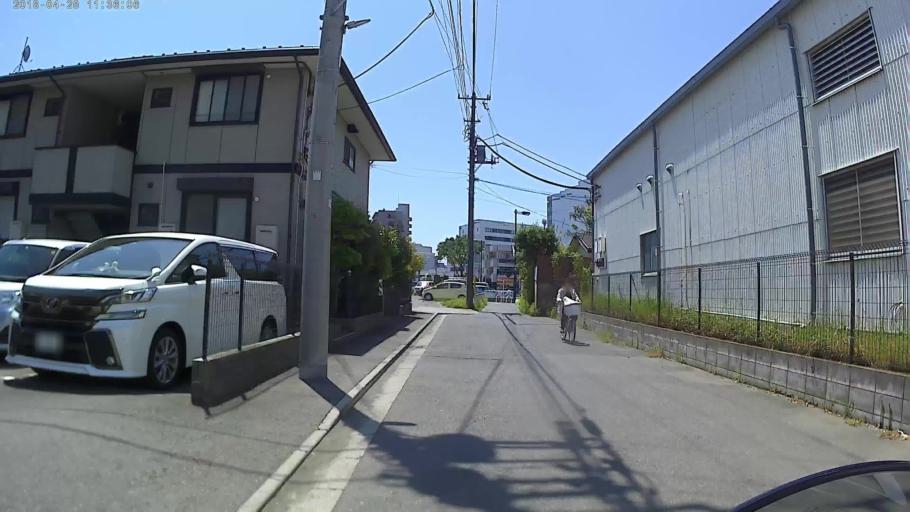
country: JP
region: Kanagawa
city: Fujisawa
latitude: 35.3422
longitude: 139.4499
